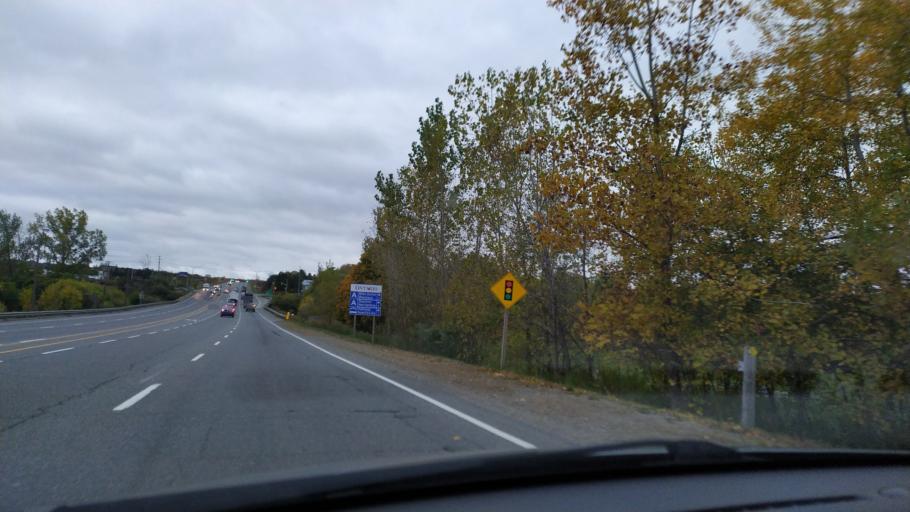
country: CA
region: Ontario
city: Kitchener
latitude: 43.3749
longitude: -80.7007
